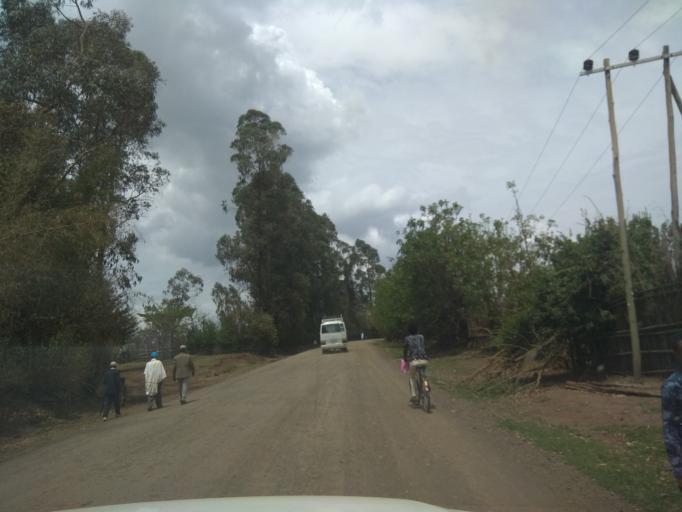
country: ET
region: Oromiya
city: Guder
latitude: 8.8088
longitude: 37.6401
